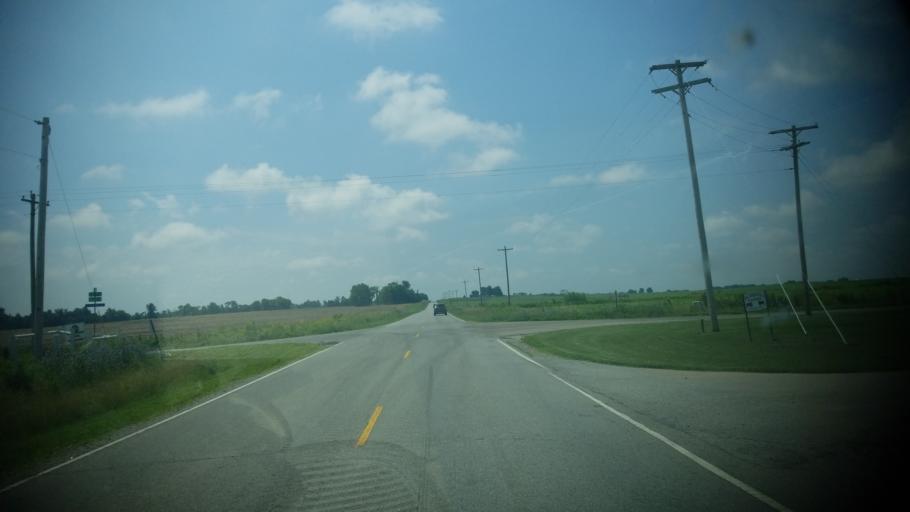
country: US
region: Illinois
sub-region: Wayne County
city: Fairfield
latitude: 38.4449
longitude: -88.3493
